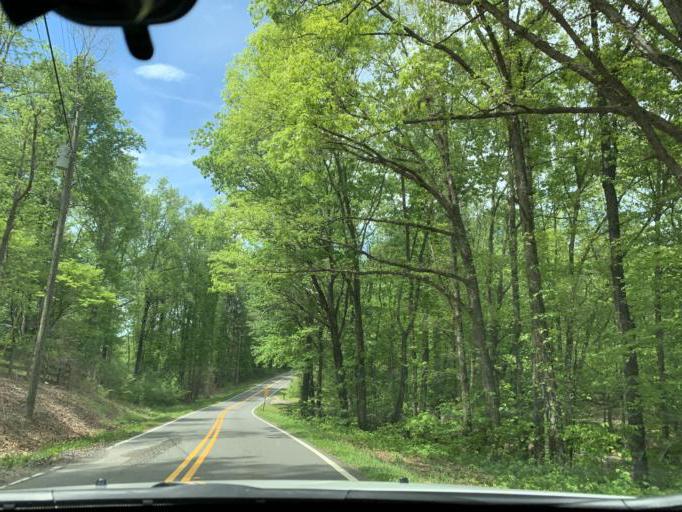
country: US
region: Georgia
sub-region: Hall County
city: Flowery Branch
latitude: 34.2724
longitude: -84.0240
